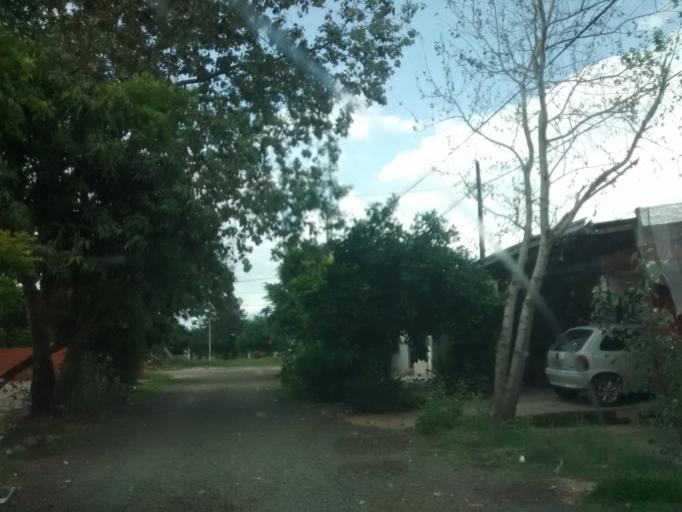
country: AR
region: Chaco
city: Resistencia
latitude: -27.4258
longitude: -58.9764
